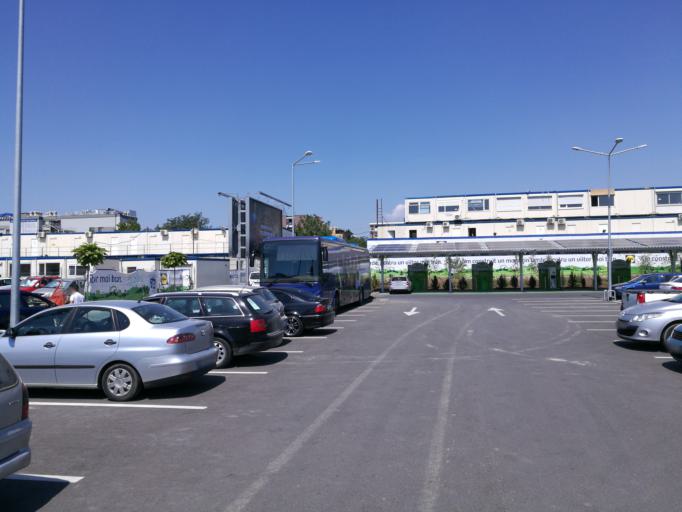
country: RO
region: Bucuresti
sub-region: Municipiul Bucuresti
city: Bucharest
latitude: 44.4884
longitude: 26.0939
